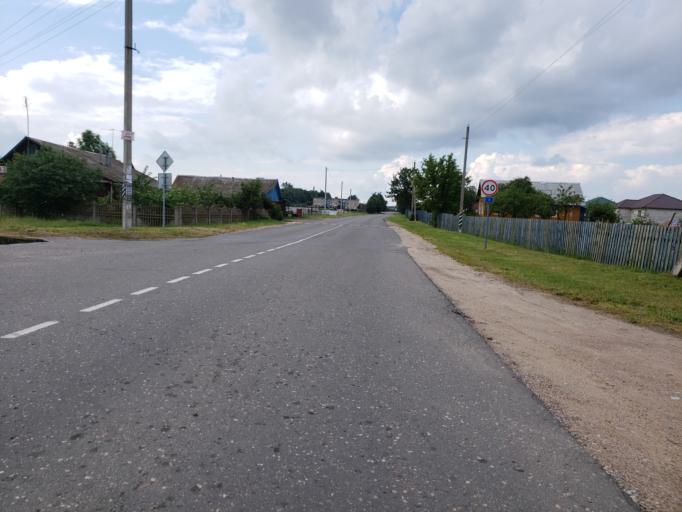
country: BY
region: Minsk
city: Chervyen'
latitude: 53.7303
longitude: 28.3882
